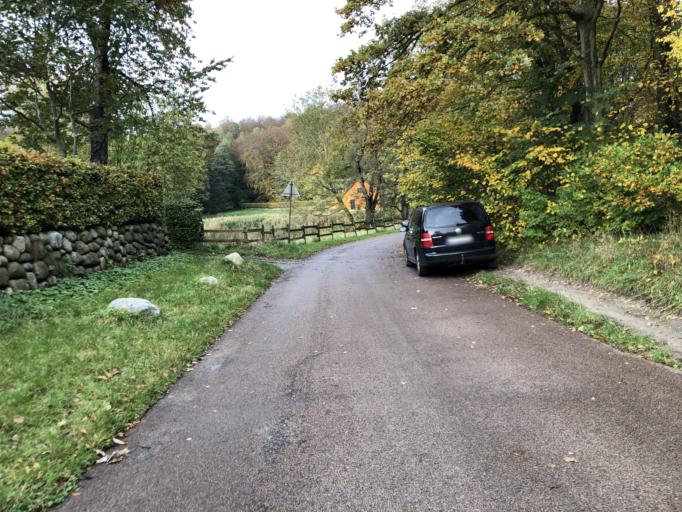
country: DK
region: Capital Region
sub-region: Lyngby-Tarbaek Kommune
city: Kongens Lyngby
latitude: 55.8009
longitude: 12.5140
